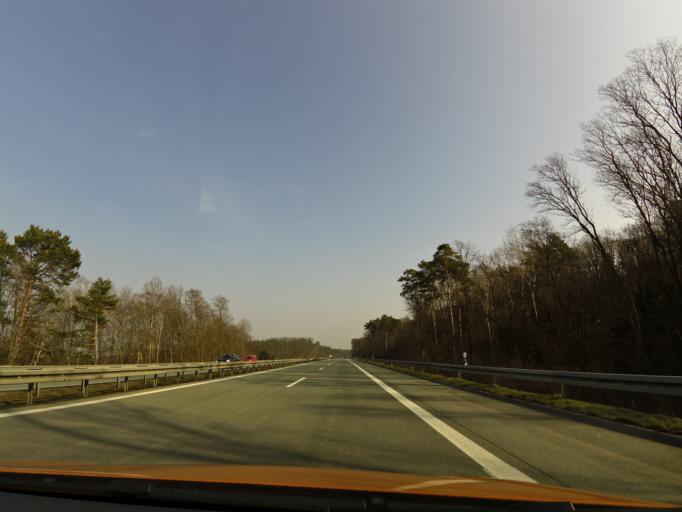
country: DE
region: Brandenburg
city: Rauen
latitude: 52.3269
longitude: 14.0328
